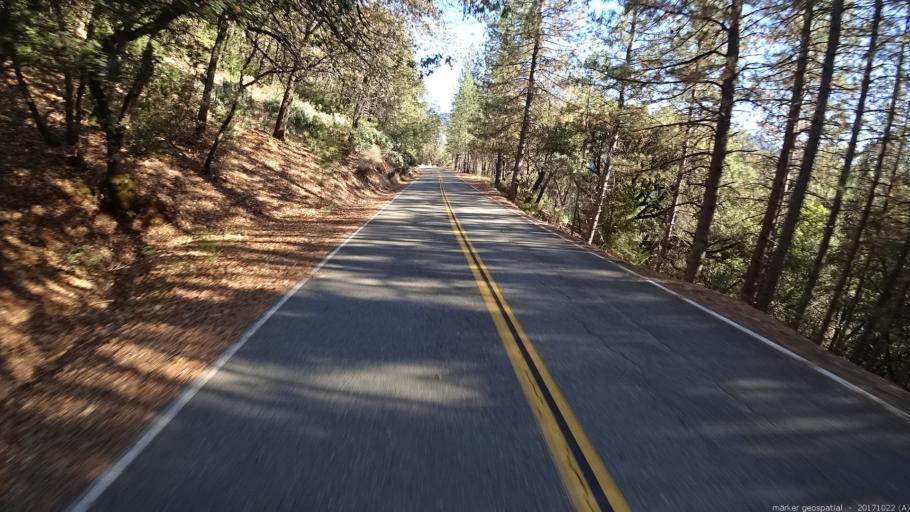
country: US
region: California
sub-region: Shasta County
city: Shasta Lake
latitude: 40.8736
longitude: -122.2454
